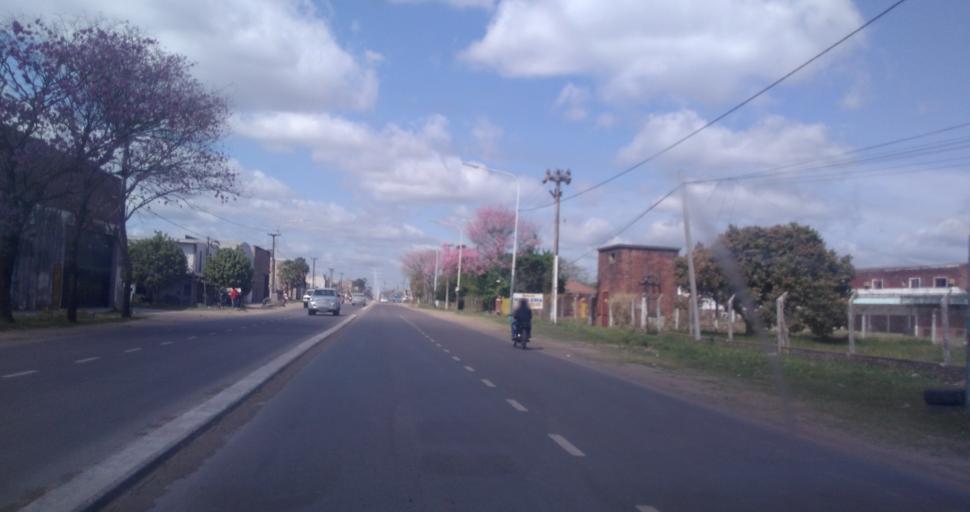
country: AR
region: Chaco
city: Fontana
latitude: -27.4299
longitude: -59.0248
